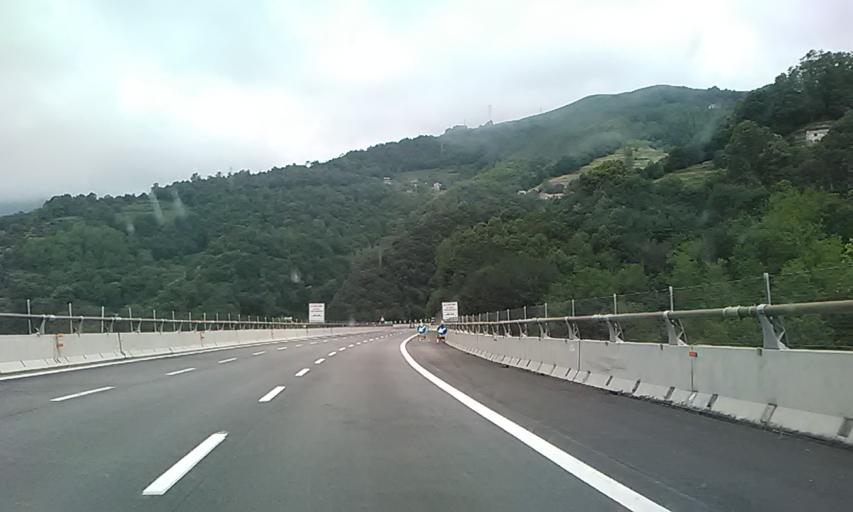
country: IT
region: Liguria
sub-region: Provincia di Genova
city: Mele
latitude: 44.4487
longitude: 8.7298
